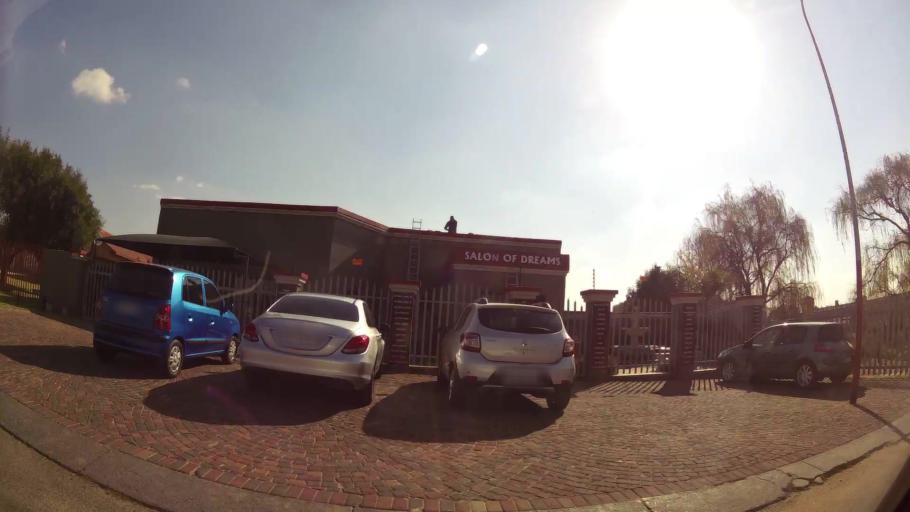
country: ZA
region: Gauteng
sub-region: Ekurhuleni Metropolitan Municipality
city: Brakpan
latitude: -26.2527
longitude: 28.3138
